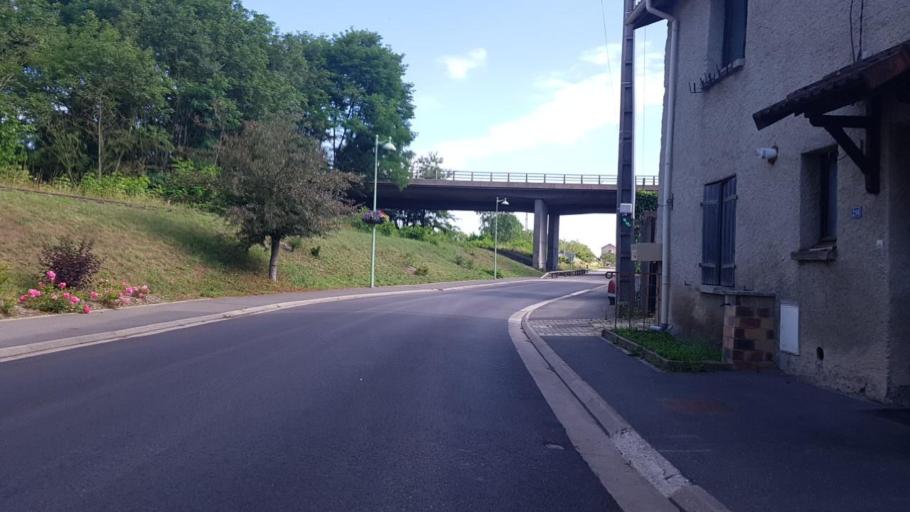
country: FR
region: Lorraine
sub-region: Departement de Meurthe-et-Moselle
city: Dommartin-les-Toul
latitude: 48.6560
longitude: 5.9022
